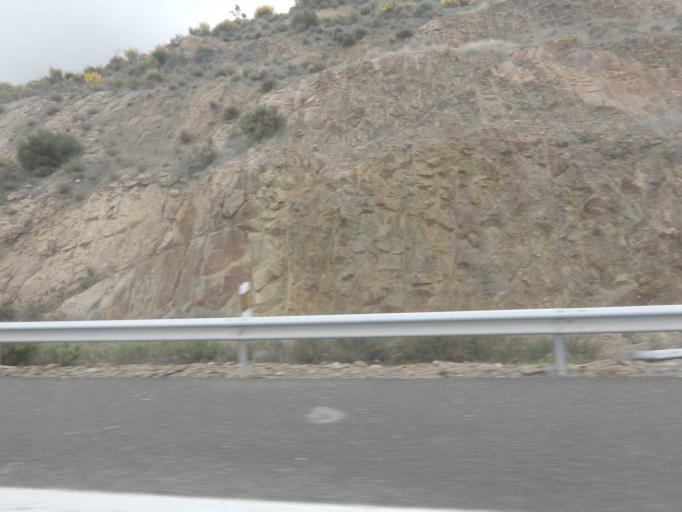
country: ES
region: Extremadura
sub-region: Provincia de Caceres
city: Banos de Montemayor
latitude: 40.3063
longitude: -5.8814
